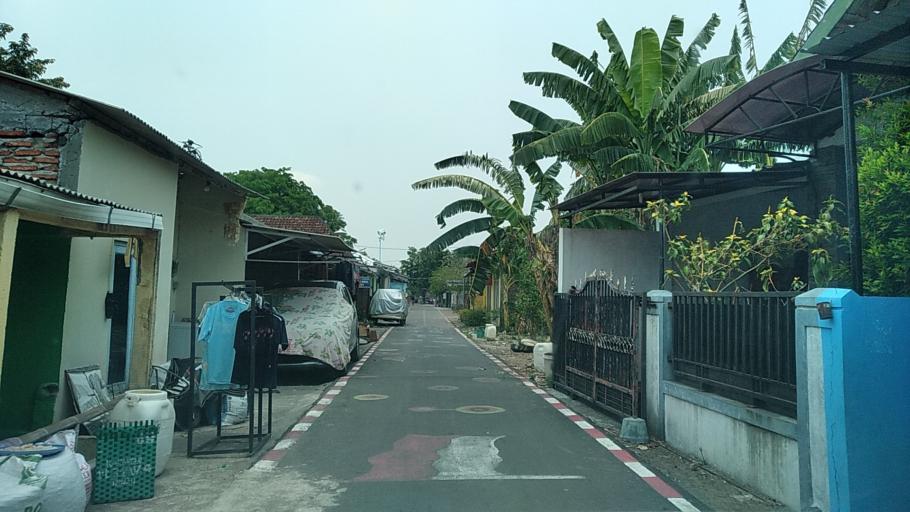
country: ID
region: Central Java
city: Mranggen
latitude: -7.0160
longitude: 110.4687
